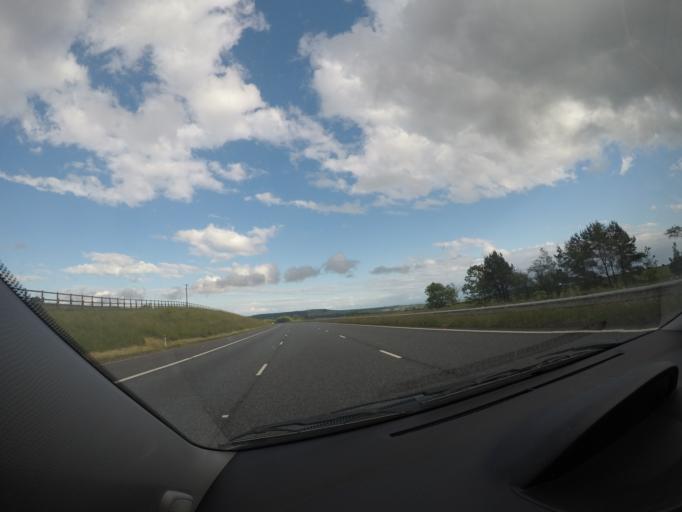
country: GB
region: Scotland
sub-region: Dumfries and Galloway
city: Lockerbie
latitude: 55.0757
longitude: -3.3071
